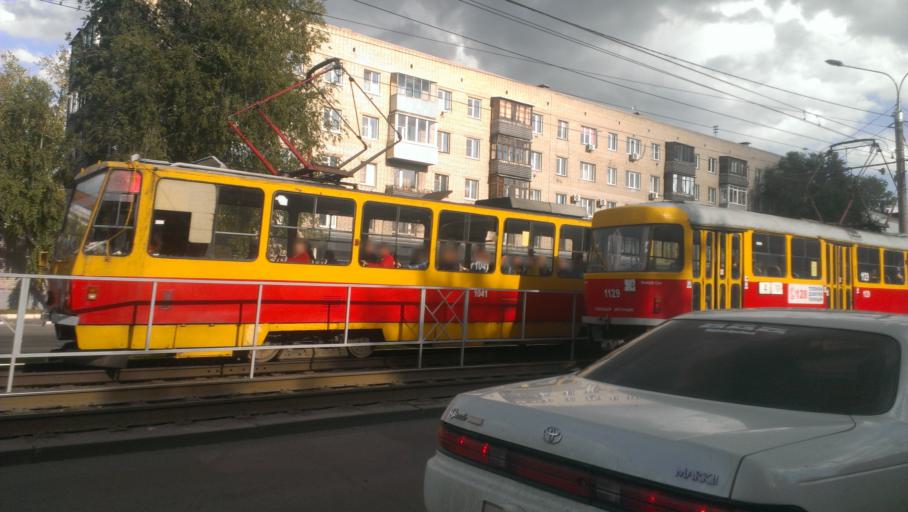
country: RU
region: Altai Krai
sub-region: Gorod Barnaulskiy
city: Barnaul
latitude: 53.3471
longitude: 83.7638
